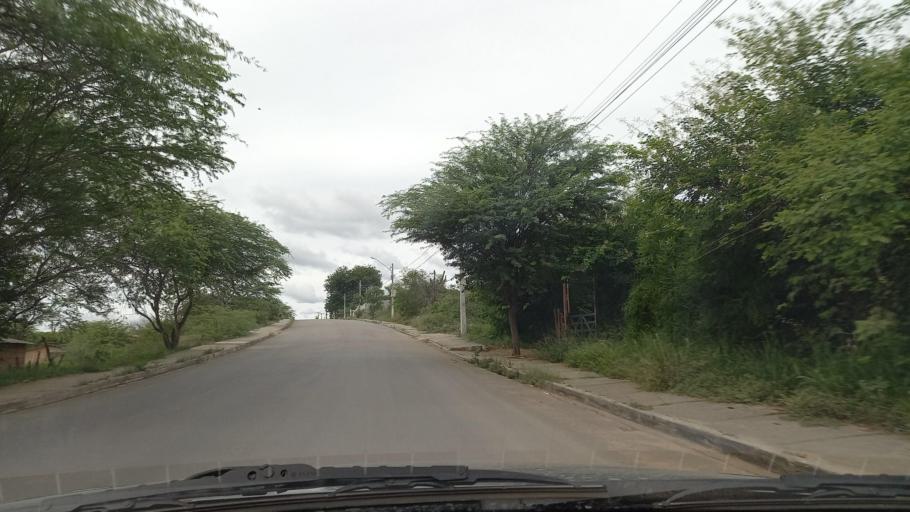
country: BR
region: Pernambuco
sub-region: Gravata
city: Gravata
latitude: -8.2142
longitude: -35.6059
